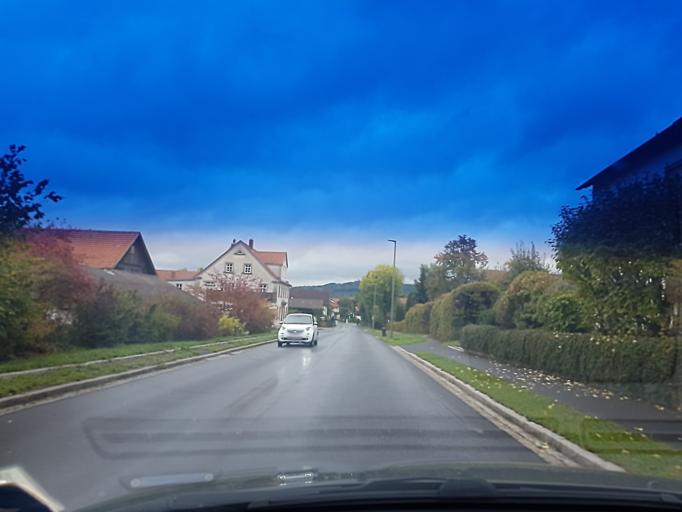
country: DE
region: Bavaria
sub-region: Upper Franconia
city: Goldkronach
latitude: 49.9941
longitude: 11.6591
